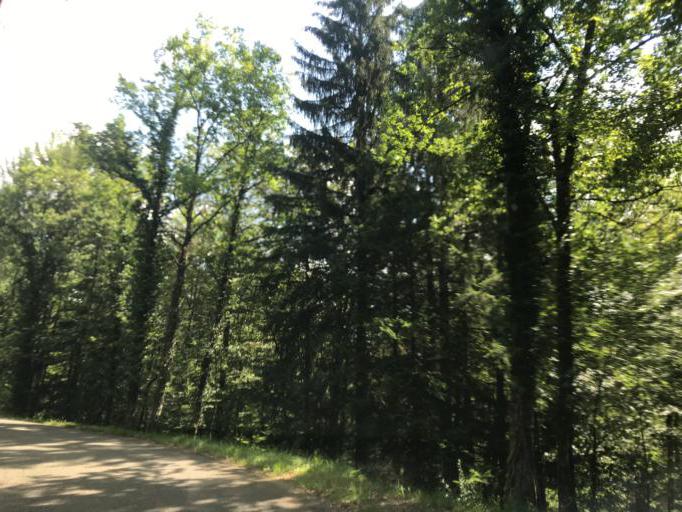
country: FR
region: Franche-Comte
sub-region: Departement du Jura
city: Moirans-en-Montagne
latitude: 46.4949
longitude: 5.7634
